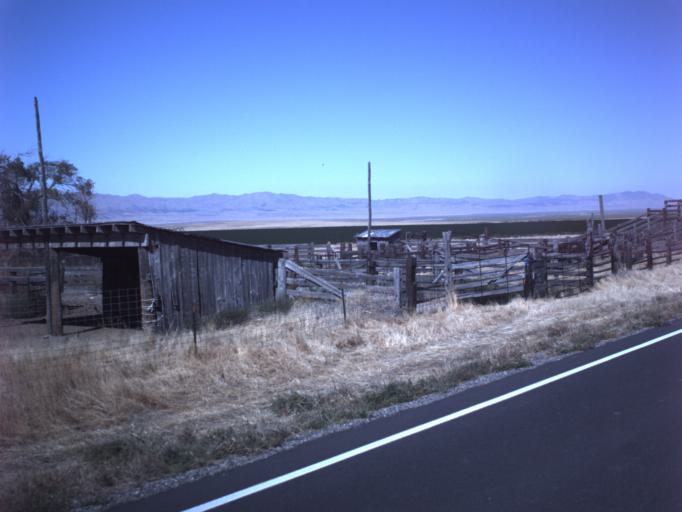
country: US
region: Utah
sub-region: Tooele County
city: Grantsville
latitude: 40.4342
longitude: -112.7487
